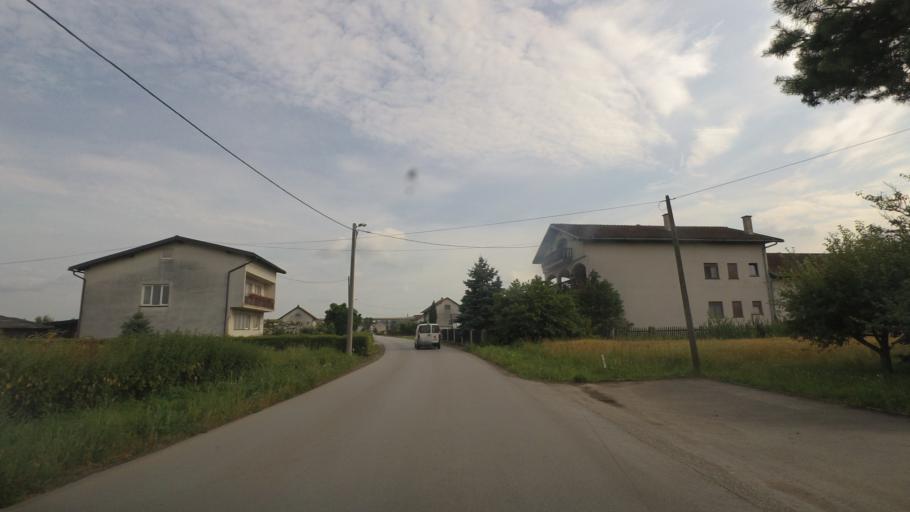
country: HR
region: Karlovacka
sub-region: Grad Karlovac
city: Karlovac
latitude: 45.5154
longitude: 15.5294
